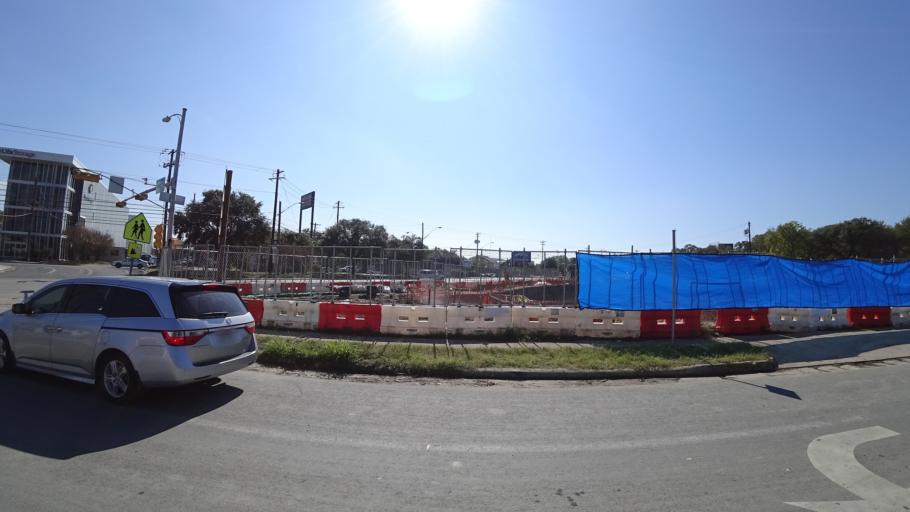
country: US
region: Texas
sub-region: Travis County
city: Austin
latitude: 30.2496
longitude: -97.7676
